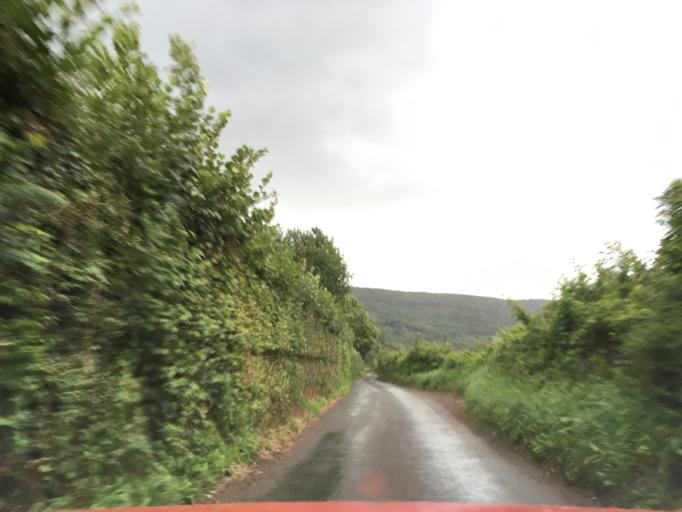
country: GB
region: Wales
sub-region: Monmouthshire
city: Llangybi
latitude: 51.6520
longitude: -2.8845
